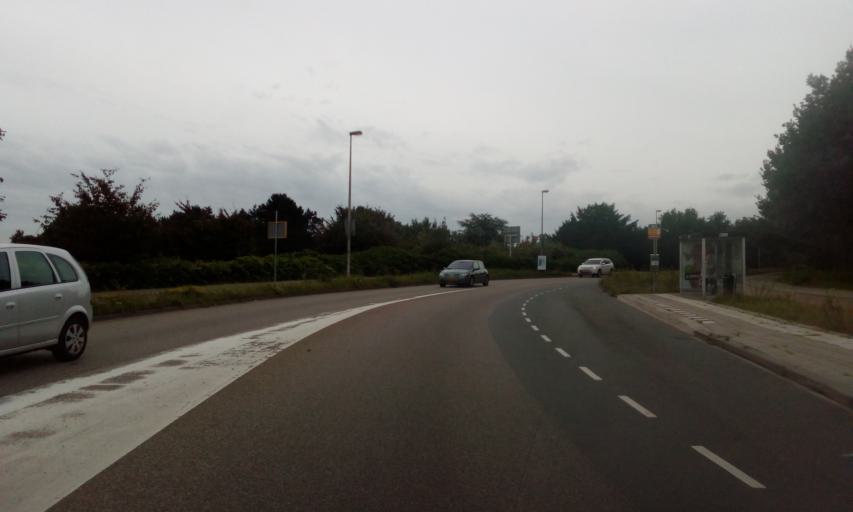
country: NL
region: North Holland
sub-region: Gemeente Bussum
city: Bussum
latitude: 52.2663
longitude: 5.1637
